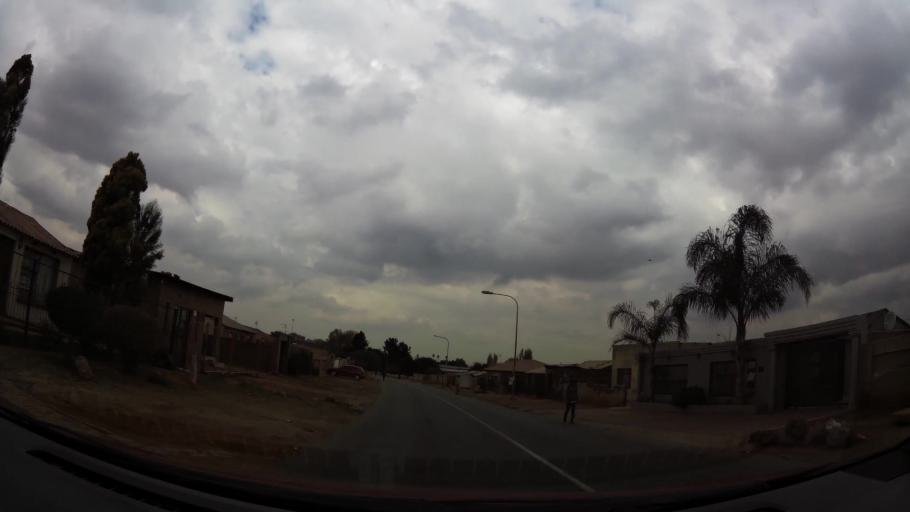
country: ZA
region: Gauteng
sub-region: City of Johannesburg Metropolitan Municipality
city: Soweto
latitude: -26.2585
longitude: 27.8431
